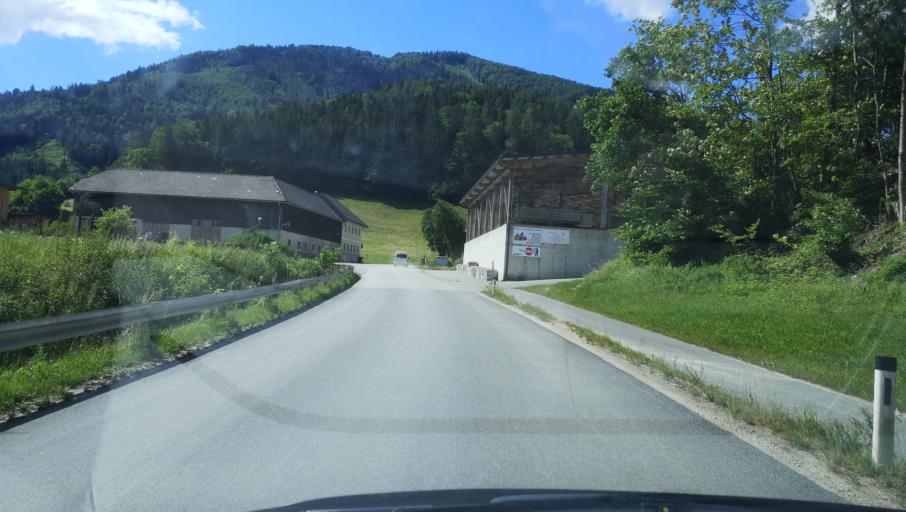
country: AT
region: Lower Austria
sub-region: Politischer Bezirk Scheibbs
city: Gresten
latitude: 47.9326
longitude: 15.0263
